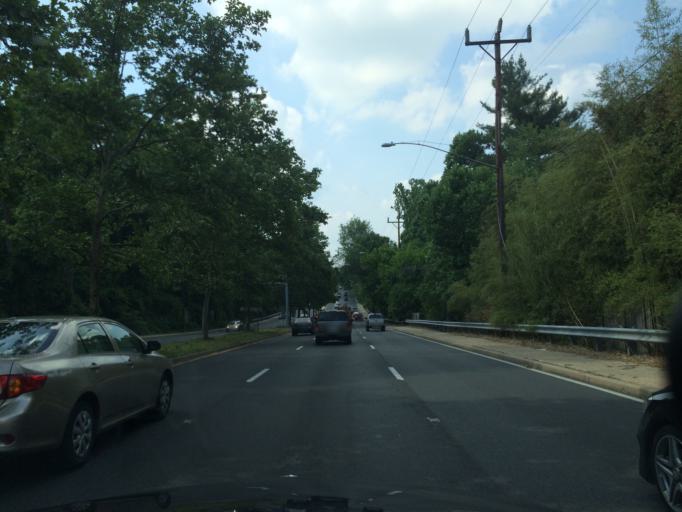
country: US
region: Maryland
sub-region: Montgomery County
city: North Kensington
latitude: 39.0396
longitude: -77.0758
